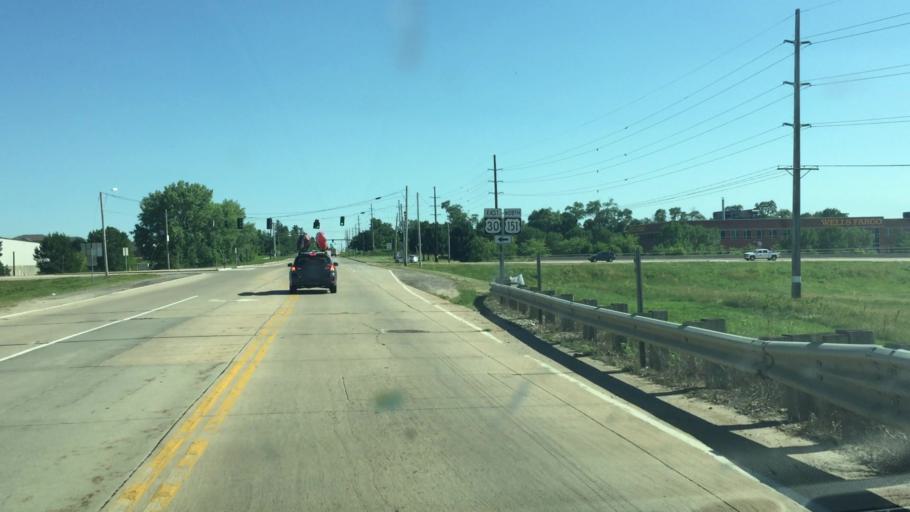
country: US
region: Iowa
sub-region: Linn County
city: Ely
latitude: 41.9261
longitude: -91.6375
